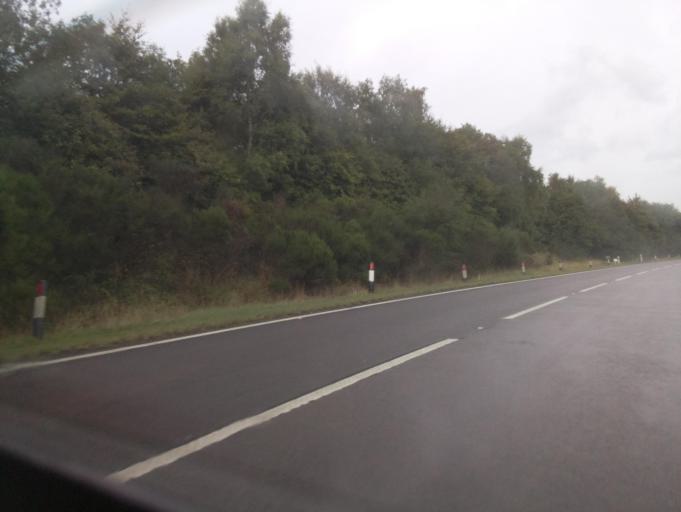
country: GB
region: Scotland
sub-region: Highland
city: Grantown on Spey
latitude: 57.2803
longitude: -3.7098
